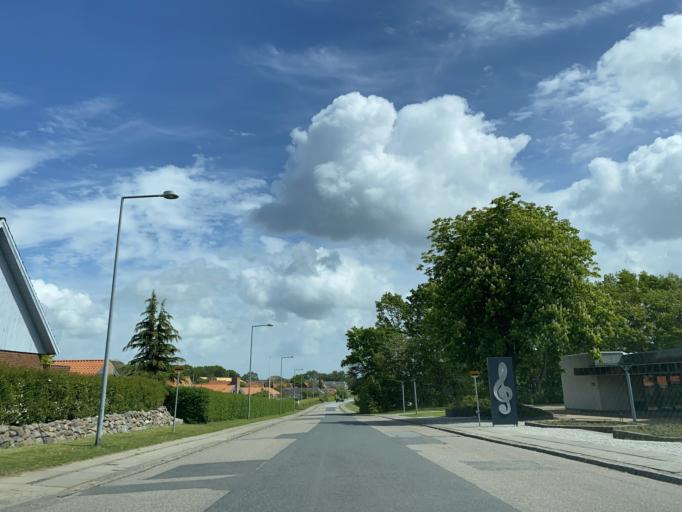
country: DK
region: South Denmark
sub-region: Sonderborg Kommune
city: Sonderborg
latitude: 54.9025
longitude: 9.8054
